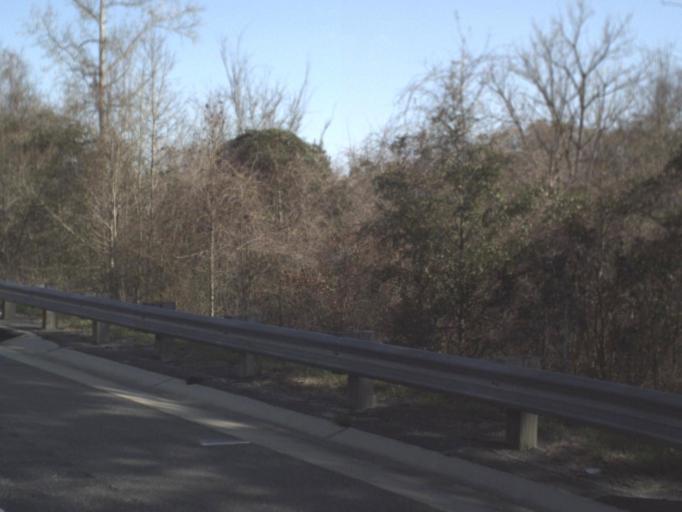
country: US
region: Florida
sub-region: Gadsden County
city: Midway
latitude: 30.5287
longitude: -84.5215
